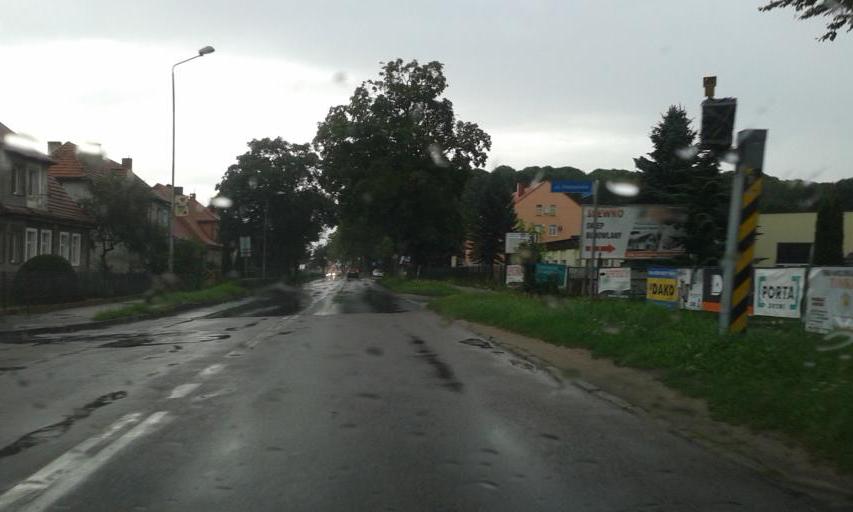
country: PL
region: West Pomeranian Voivodeship
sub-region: Powiat drawski
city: Czaplinek
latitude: 53.5524
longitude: 16.2396
